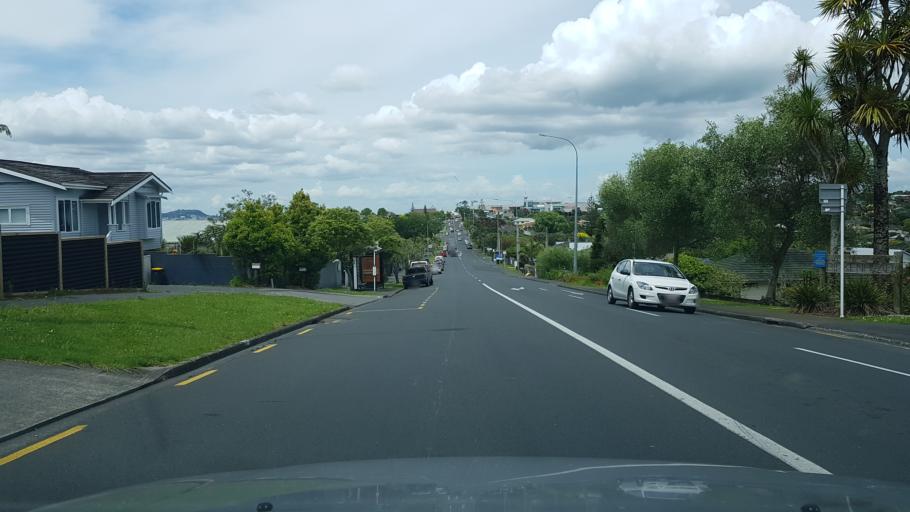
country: NZ
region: Auckland
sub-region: Auckland
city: North Shore
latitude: -36.8037
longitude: 174.7253
